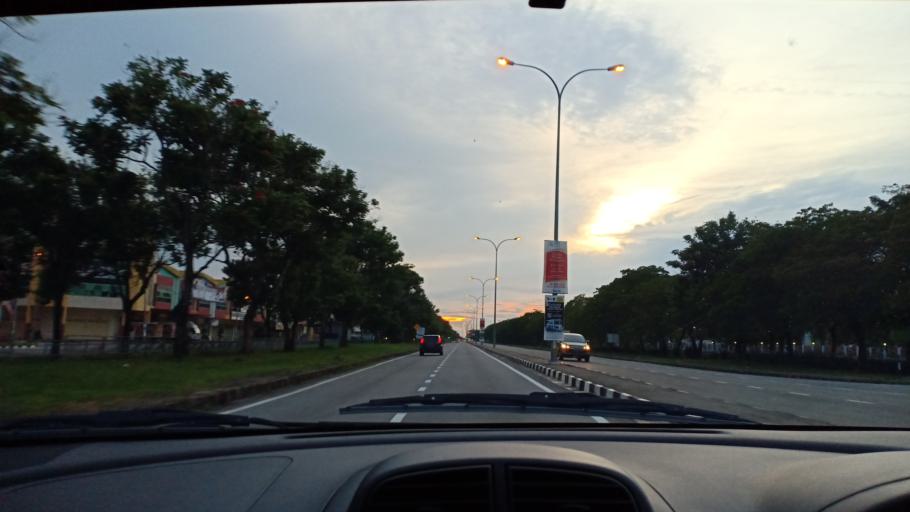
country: MY
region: Penang
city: Tasek Glugor
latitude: 5.5201
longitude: 100.4809
